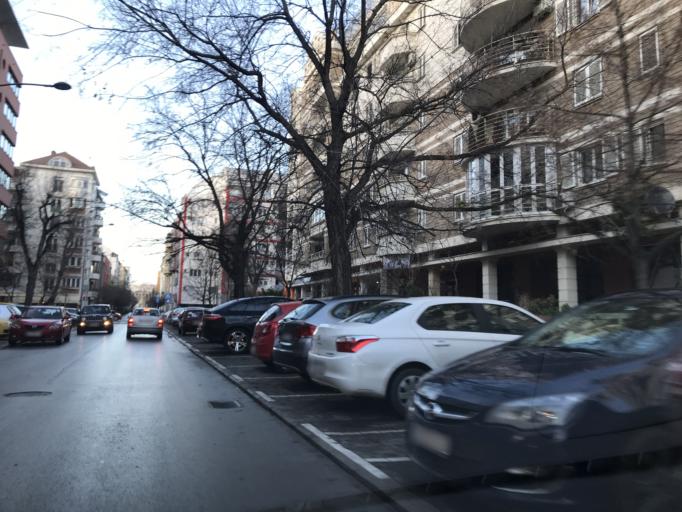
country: RS
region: Autonomna Pokrajina Vojvodina
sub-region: Juznobacki Okrug
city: Novi Sad
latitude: 45.2495
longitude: 19.8520
